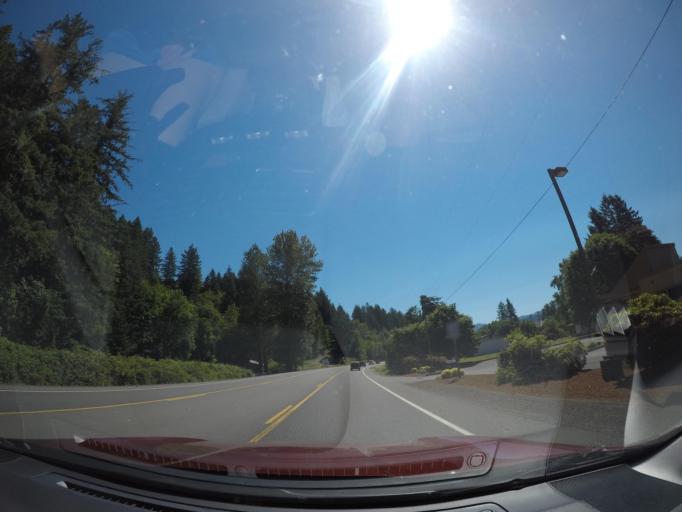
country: US
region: Oregon
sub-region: Linn County
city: Mill City
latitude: 44.7572
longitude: -122.4815
